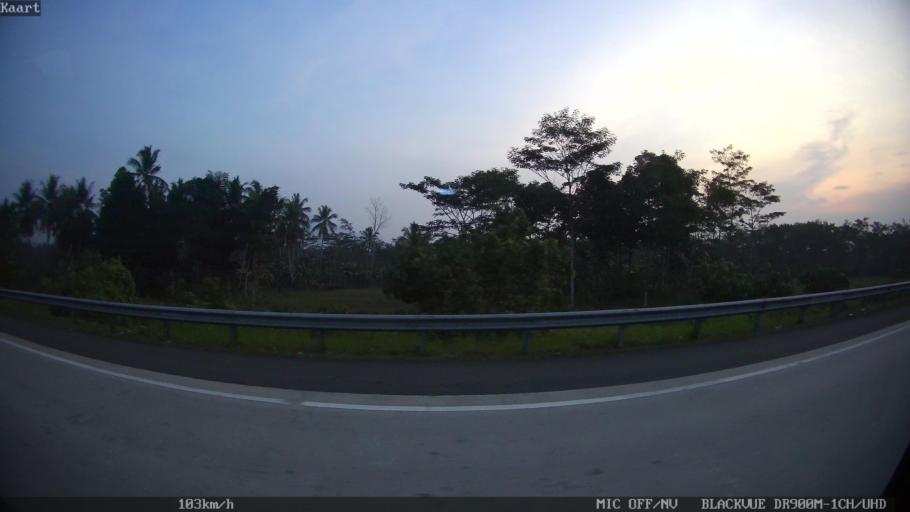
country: ID
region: Lampung
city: Pasuruan
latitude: -5.7079
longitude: 105.6431
